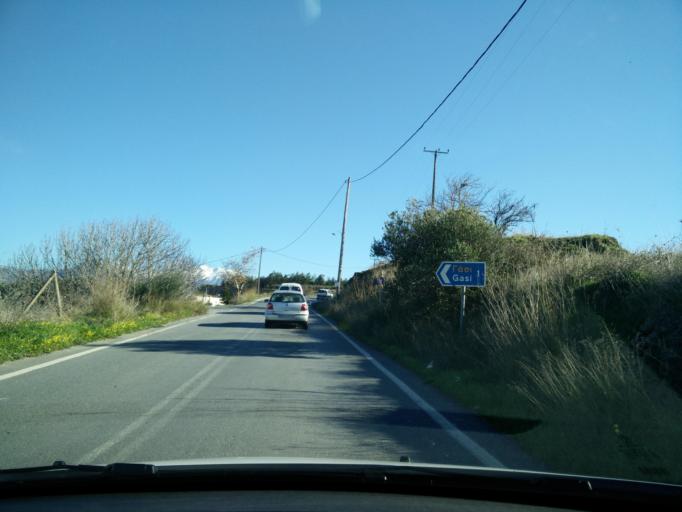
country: GR
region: Crete
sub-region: Nomos Irakleiou
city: Arkalochori
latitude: 35.1356
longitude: 25.2635
